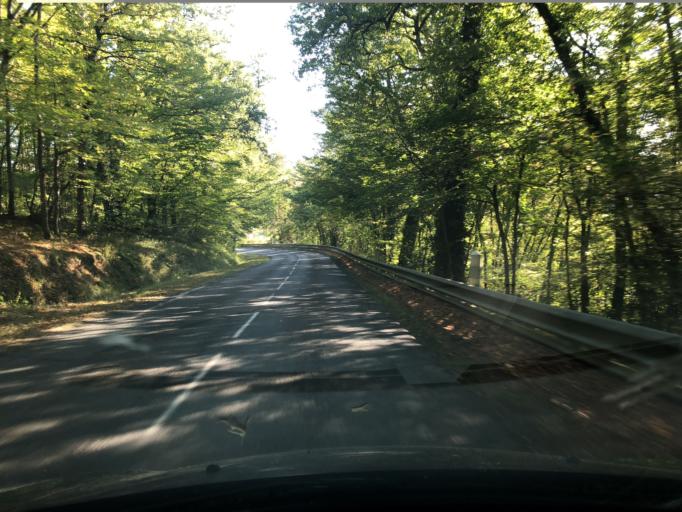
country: FR
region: Centre
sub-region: Departement d'Indre-et-Loire
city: Neuvy-le-Roi
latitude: 47.5862
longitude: 0.5958
